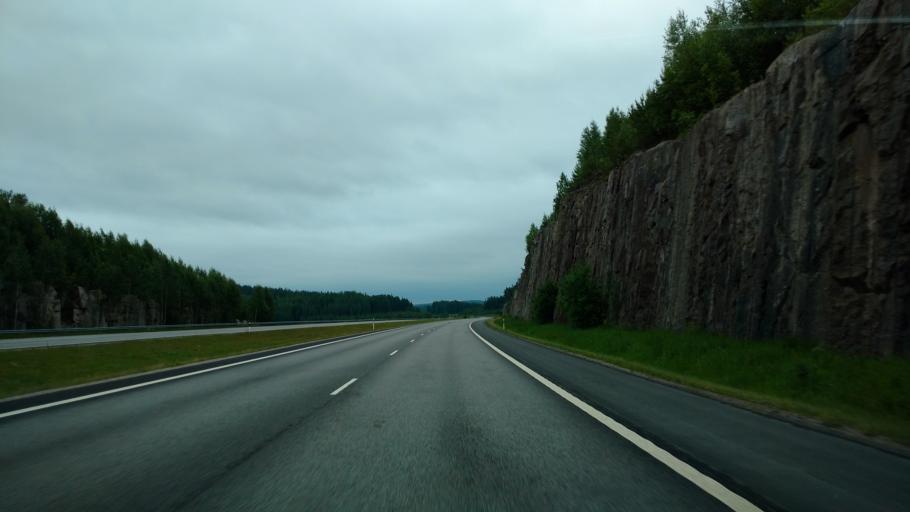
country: FI
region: Varsinais-Suomi
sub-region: Salo
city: Pertteli
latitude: 60.3965
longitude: 23.2547
